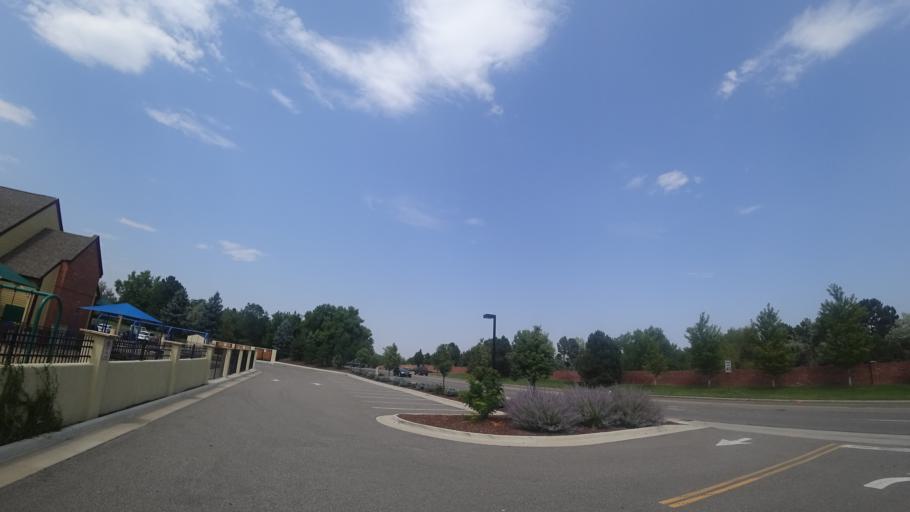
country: US
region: Colorado
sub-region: Arapahoe County
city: Greenwood Village
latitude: 39.6107
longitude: -104.9603
